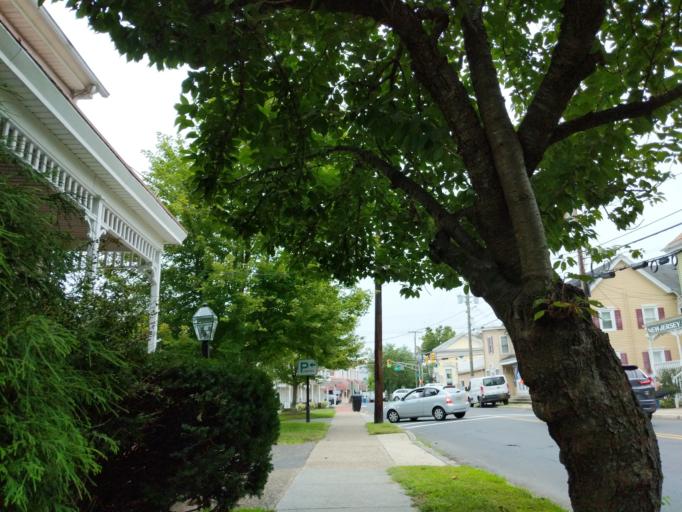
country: US
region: New Jersey
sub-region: Burlington County
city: Medford Lakes
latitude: 39.8995
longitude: -74.8245
